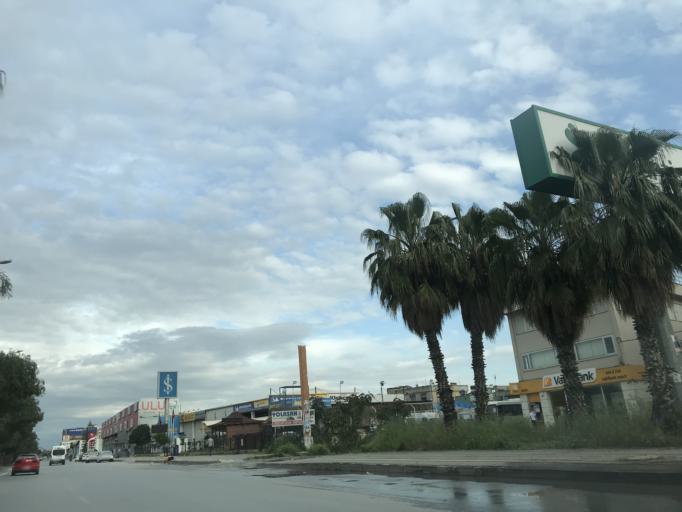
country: TR
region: Adana
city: Seyhan
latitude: 36.9948
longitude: 35.2799
